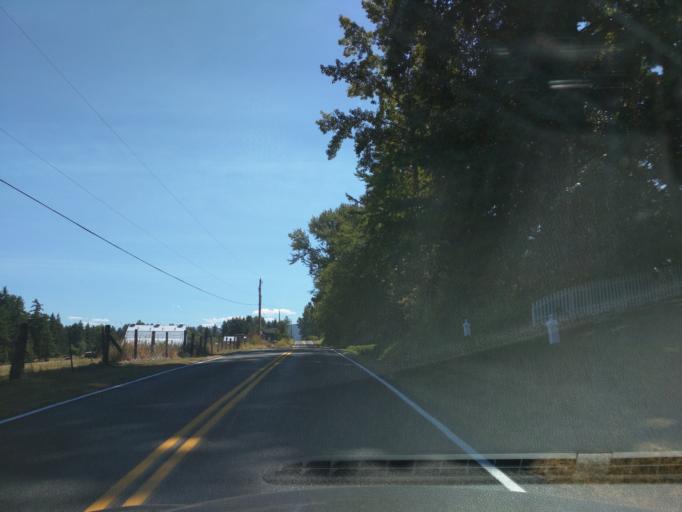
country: US
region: Washington
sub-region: Whatcom County
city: Geneva
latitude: 48.8041
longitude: -122.4041
